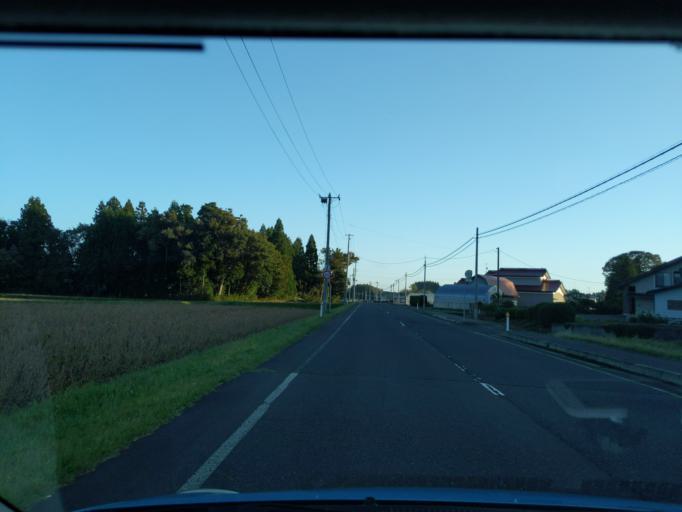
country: JP
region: Iwate
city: Mizusawa
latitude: 39.0800
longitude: 141.0928
